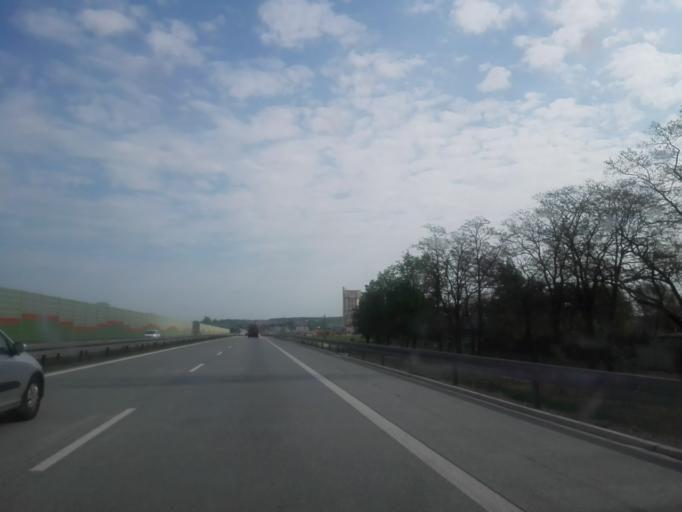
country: PL
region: Lodz Voivodeship
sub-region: Powiat rawski
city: Rawa Mazowiecka
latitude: 51.7585
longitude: 20.2606
